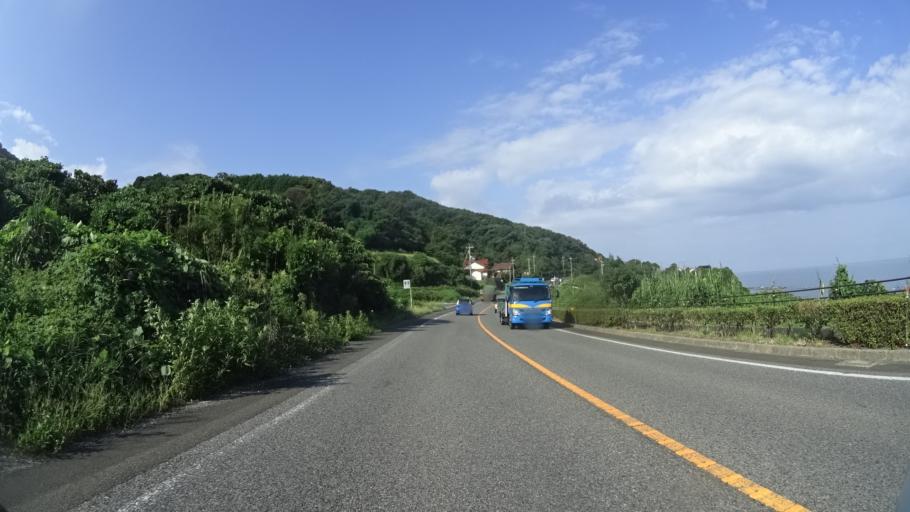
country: JP
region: Shimane
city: Odacho-oda
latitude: 35.2754
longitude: 132.5979
